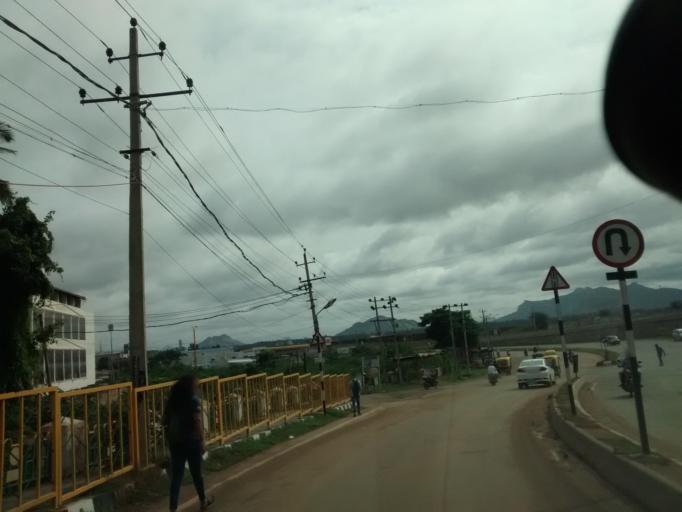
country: IN
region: Karnataka
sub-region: Tumkur
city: Tumkur
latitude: 13.3489
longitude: 77.1023
